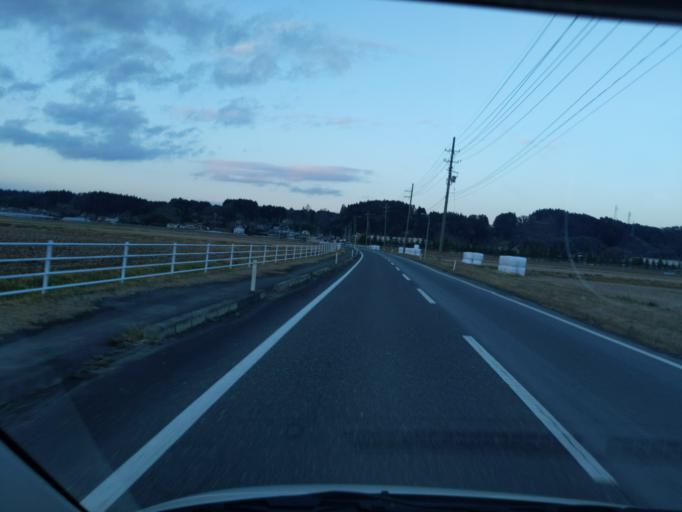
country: JP
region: Iwate
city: Ichinoseki
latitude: 38.7963
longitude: 141.1216
